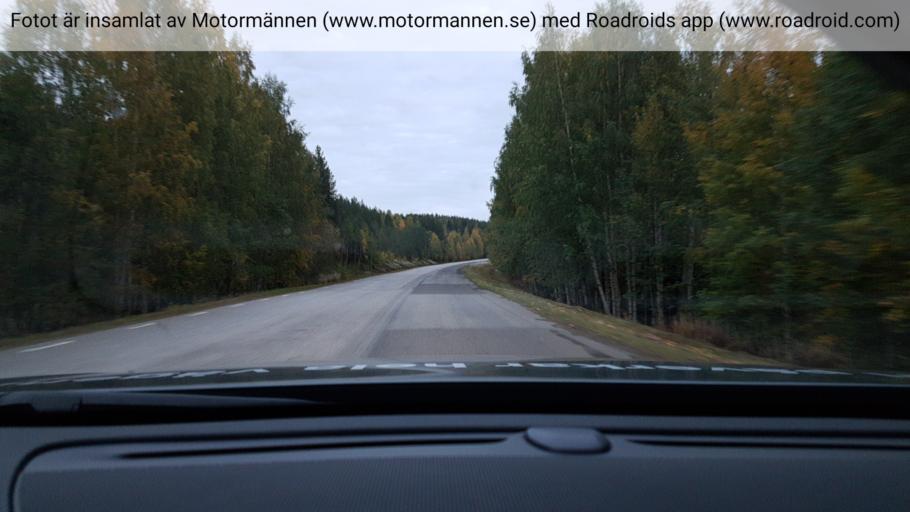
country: SE
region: Norrbotten
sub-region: Alvsbyns Kommun
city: AElvsbyn
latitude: 65.8526
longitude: 20.4454
